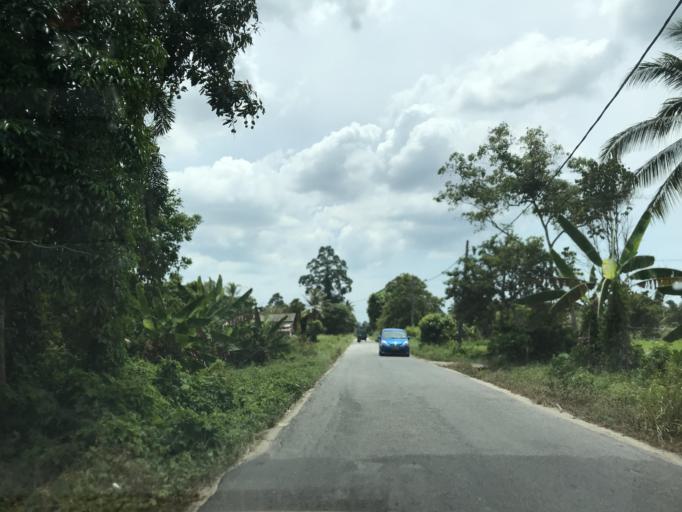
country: MY
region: Kelantan
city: Kota Bharu
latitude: 6.1408
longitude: 102.1857
